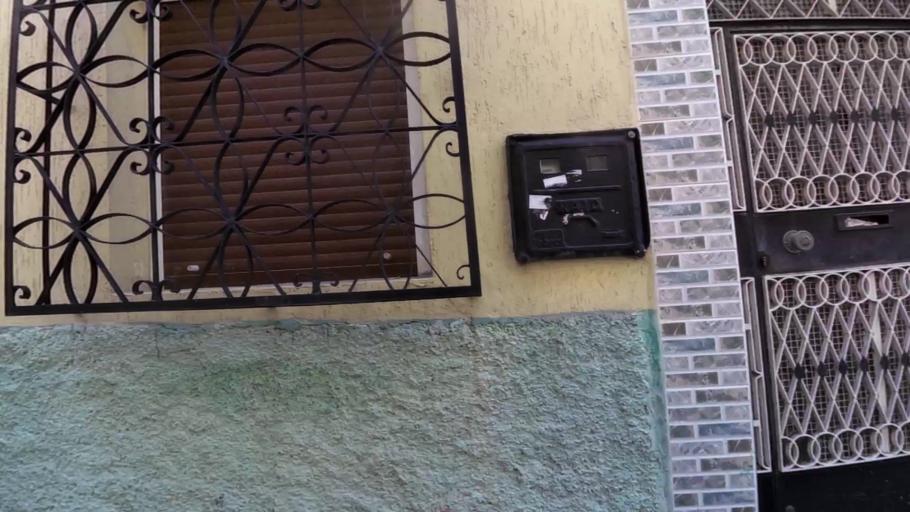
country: MA
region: Tanger-Tetouan
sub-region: Tanger-Assilah
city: Tangier
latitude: 35.7560
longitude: -5.8036
